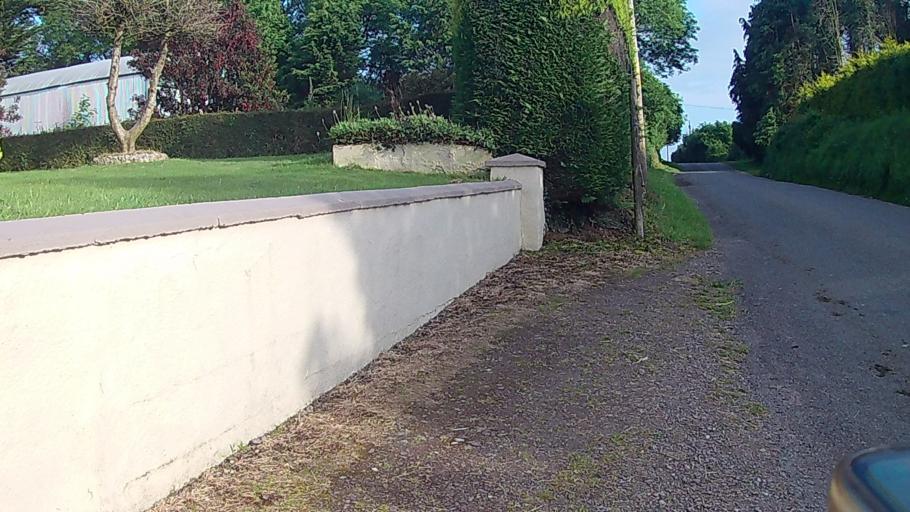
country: IE
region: Munster
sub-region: County Cork
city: Cork
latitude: 51.9857
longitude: -8.4581
